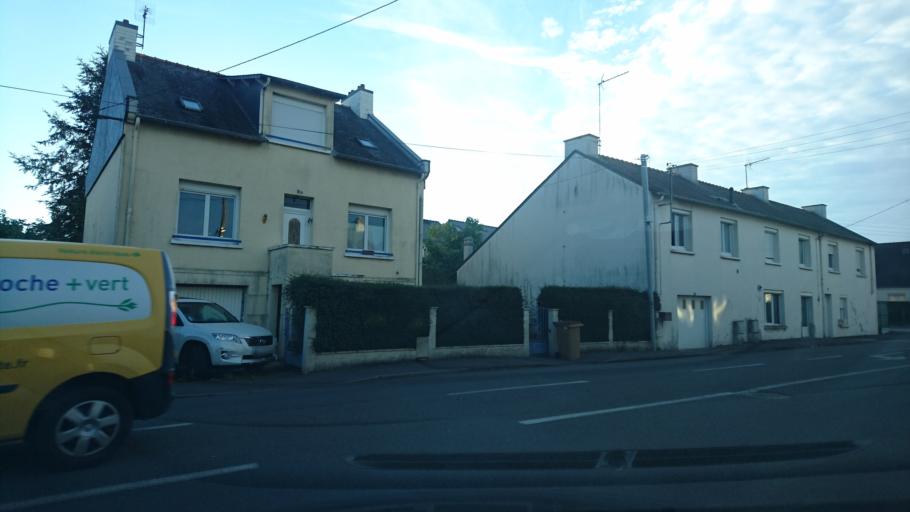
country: FR
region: Brittany
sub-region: Departement d'Ille-et-Vilaine
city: Redon
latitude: 47.6586
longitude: -2.0720
